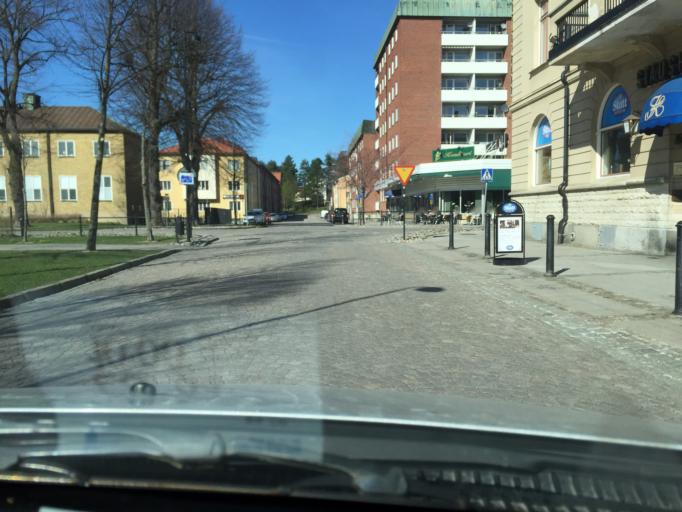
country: SE
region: Soedermanland
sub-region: Katrineholms Kommun
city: Katrineholm
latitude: 58.9971
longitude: 16.2085
